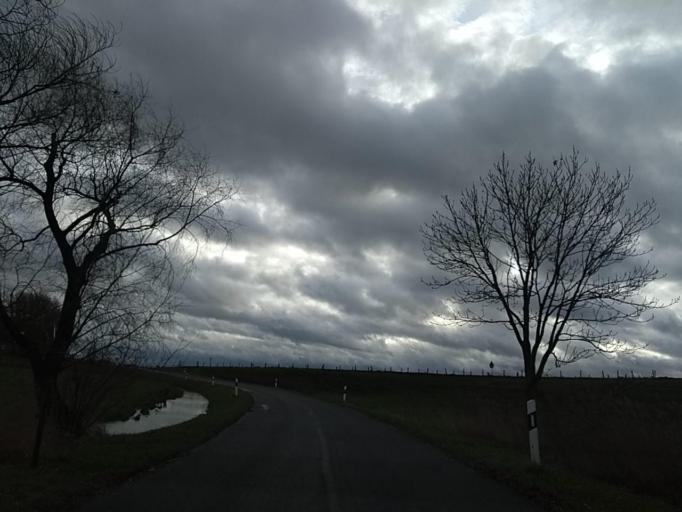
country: DE
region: Lower Saxony
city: Emden
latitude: 53.2916
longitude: 7.2463
